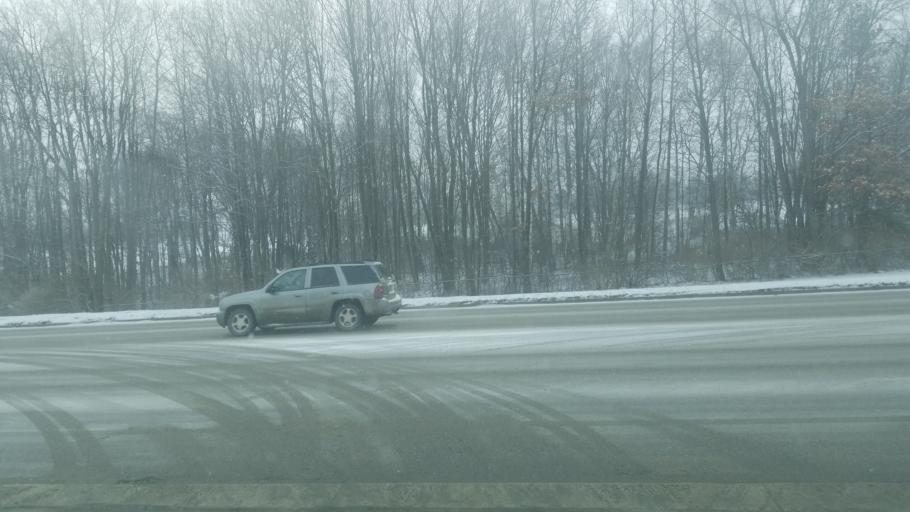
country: US
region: Michigan
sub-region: Mecosta County
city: Big Rapids
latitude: 43.6886
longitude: -85.5092
